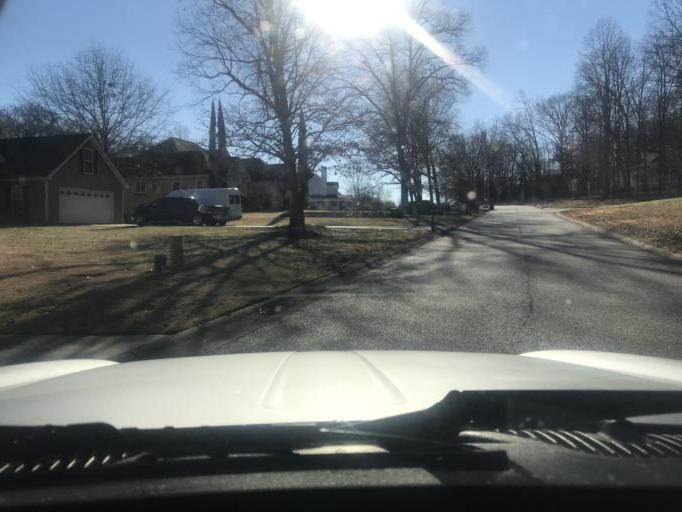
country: US
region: Georgia
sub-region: Barrow County
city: Winder
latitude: 34.0167
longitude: -83.7614
